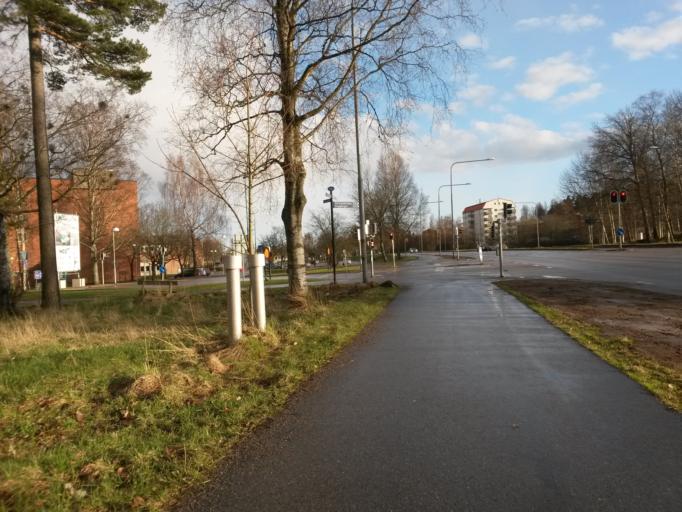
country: SE
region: OErebro
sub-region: Karlskoga Kommun
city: Karlskoga
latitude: 59.3172
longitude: 14.5035
